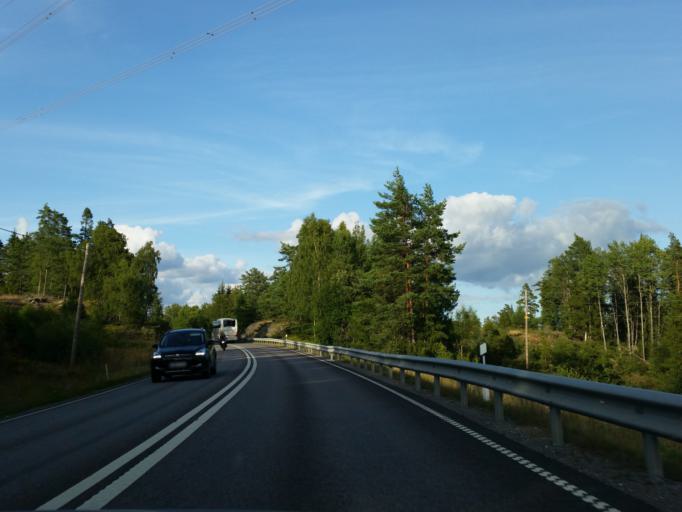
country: SE
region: Stockholm
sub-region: Sodertalje Kommun
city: Molnbo
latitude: 59.0553
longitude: 17.4619
